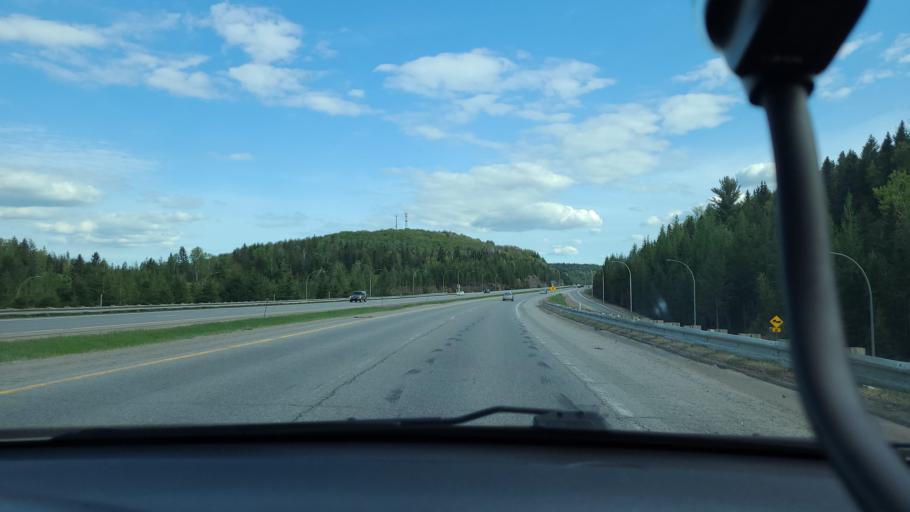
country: CA
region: Quebec
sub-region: Laurentides
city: Val-David
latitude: 46.0105
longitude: -74.2310
